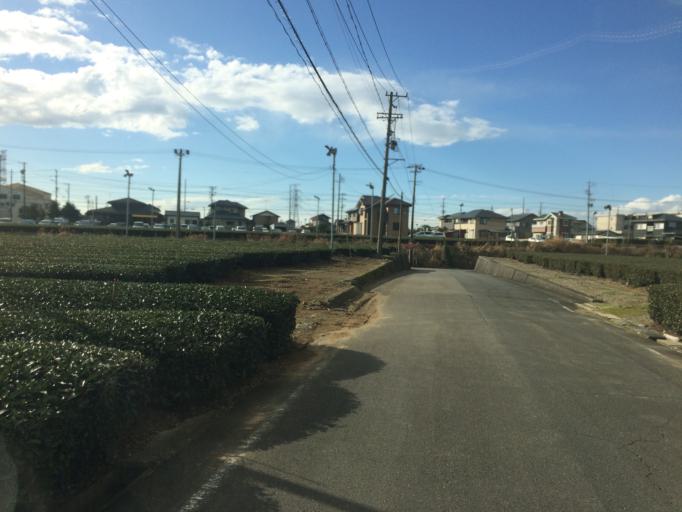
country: JP
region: Shizuoka
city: Kanaya
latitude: 34.7645
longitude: 138.1467
